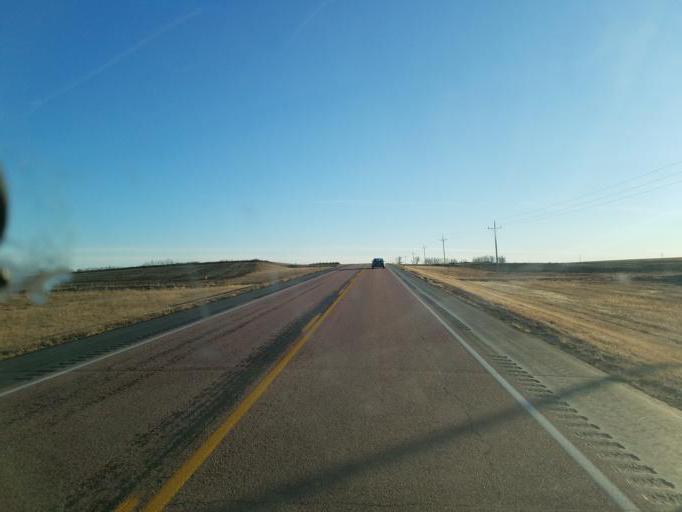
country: US
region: South Dakota
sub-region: Bon Homme County
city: Tyndall
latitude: 43.0769
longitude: -97.9702
